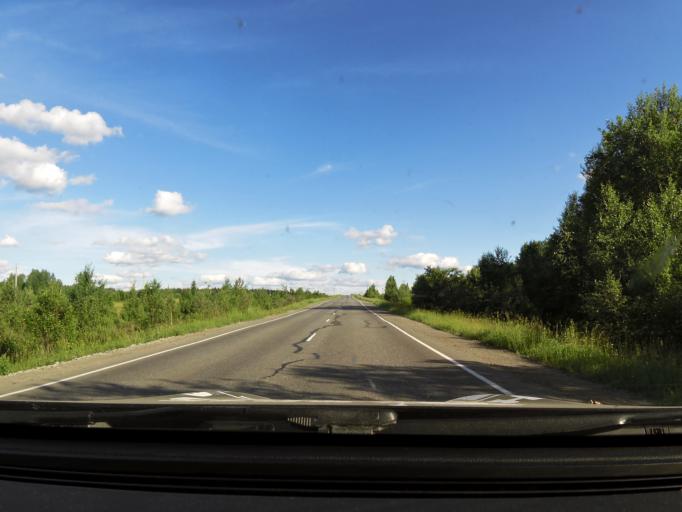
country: RU
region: Kirov
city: Omutninsk
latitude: 58.6927
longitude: 52.1303
